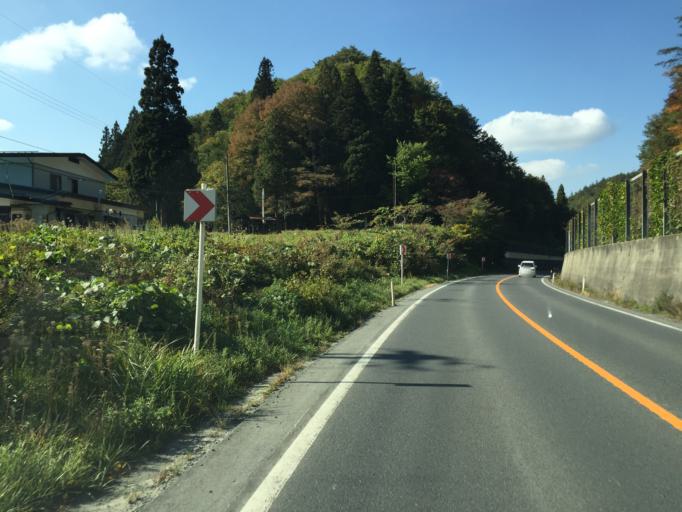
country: JP
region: Yamagata
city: Yonezawa
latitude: 37.8720
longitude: 140.2077
